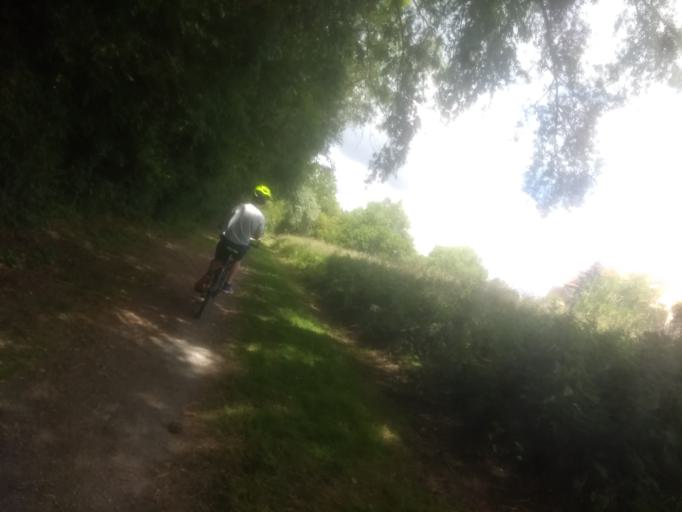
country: FR
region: Nord-Pas-de-Calais
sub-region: Departement du Pas-de-Calais
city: Sainte-Catherine
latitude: 50.3038
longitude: 2.7548
